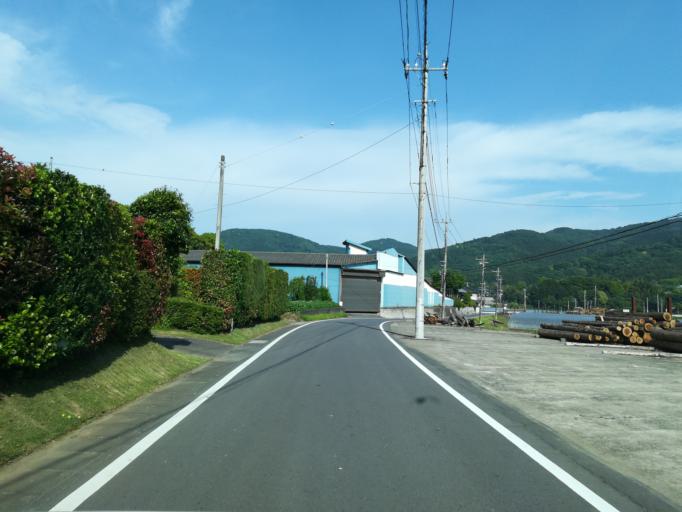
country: JP
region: Ibaraki
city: Tsukuba
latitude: 36.1890
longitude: 140.1672
